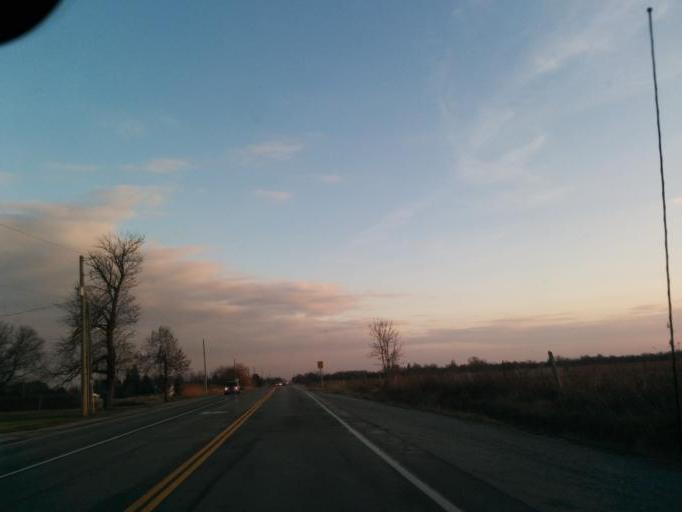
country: CA
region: Ontario
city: Brampton
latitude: 43.8590
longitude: -79.7810
